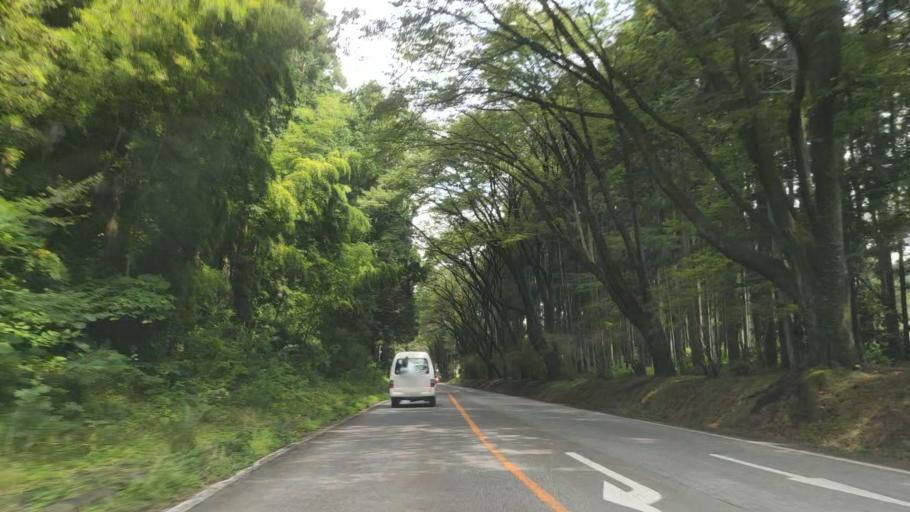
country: JP
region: Tochigi
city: Imaichi
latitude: 36.6801
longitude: 139.7940
